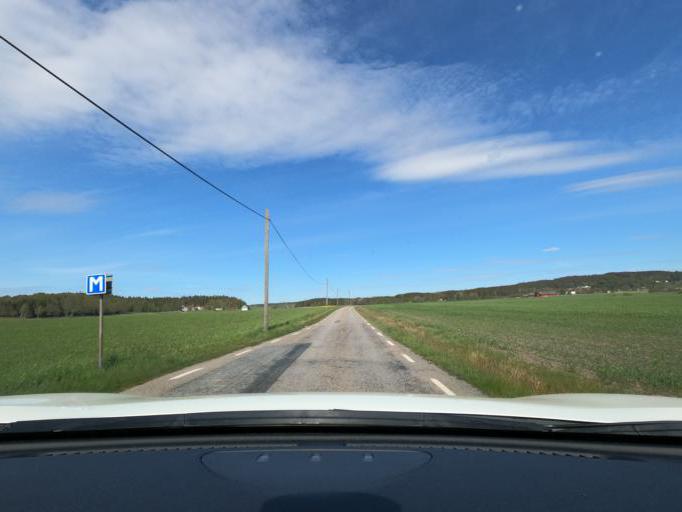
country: SE
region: Vaestra Goetaland
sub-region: Marks Kommun
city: Horred
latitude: 57.4549
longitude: 12.4904
